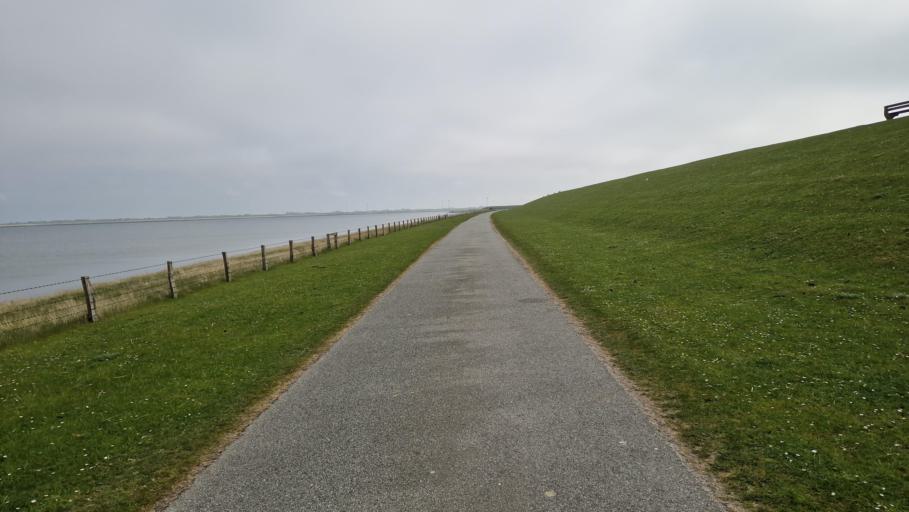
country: DE
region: Schleswig-Holstein
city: Elisabeth-Sophien-Koog
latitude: 54.5475
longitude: 8.8788
